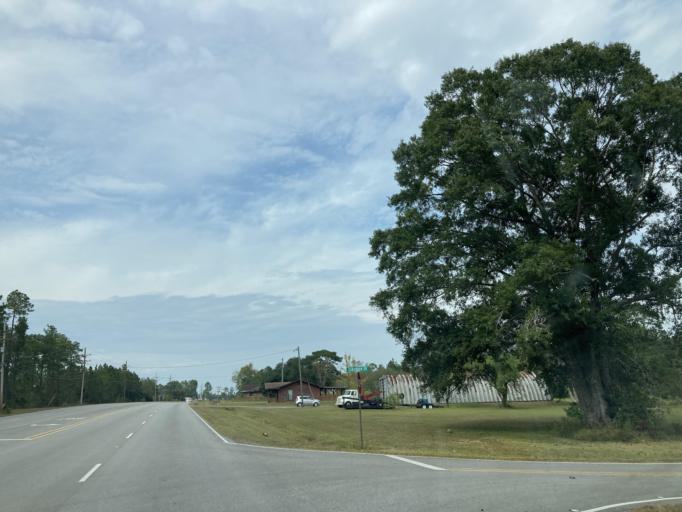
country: US
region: Mississippi
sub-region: Jackson County
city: Saint Martin
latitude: 30.4714
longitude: -88.8486
